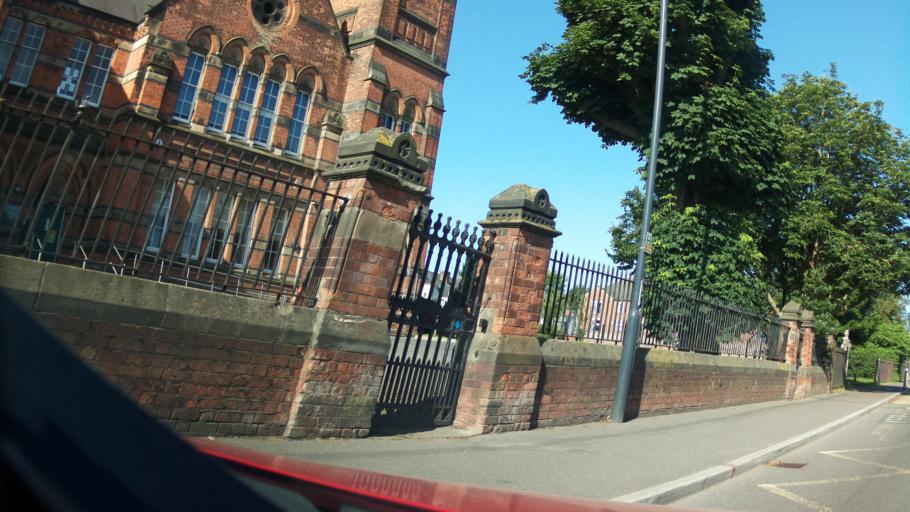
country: GB
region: England
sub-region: Derby
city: Derby
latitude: 52.9265
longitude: -1.4954
